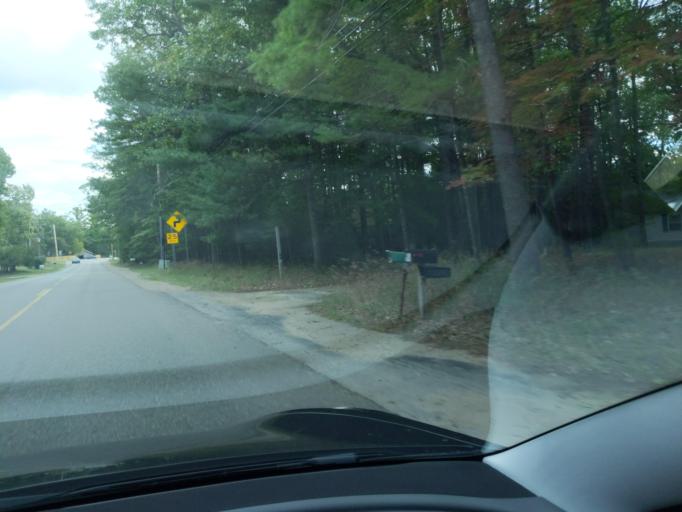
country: US
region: Michigan
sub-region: Kalkaska County
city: Rapid City
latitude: 44.8474
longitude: -85.3090
